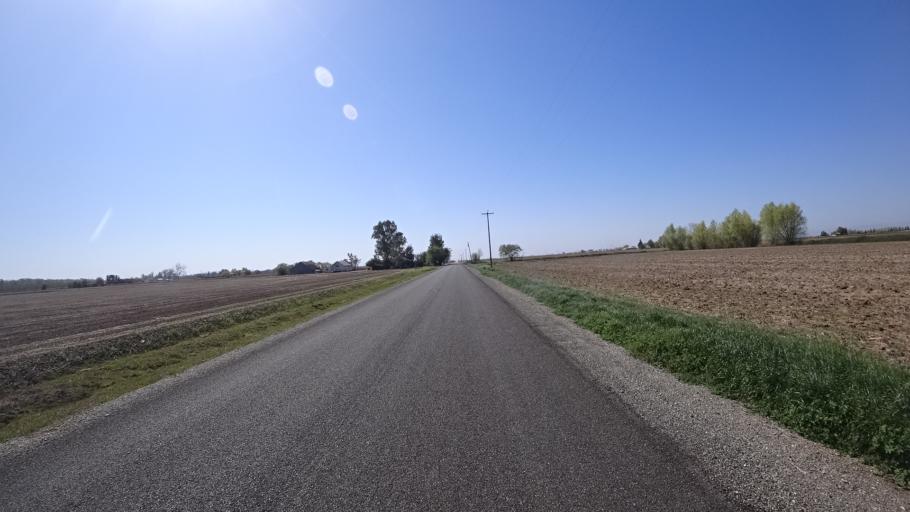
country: US
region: California
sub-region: Glenn County
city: Willows
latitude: 39.4553
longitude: -122.0314
